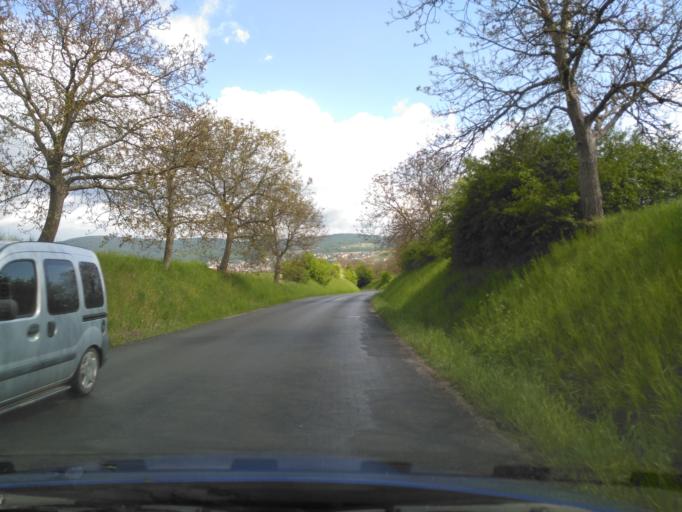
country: CZ
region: Central Bohemia
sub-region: Okres Beroun
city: Beroun
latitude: 49.9454
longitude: 14.0697
